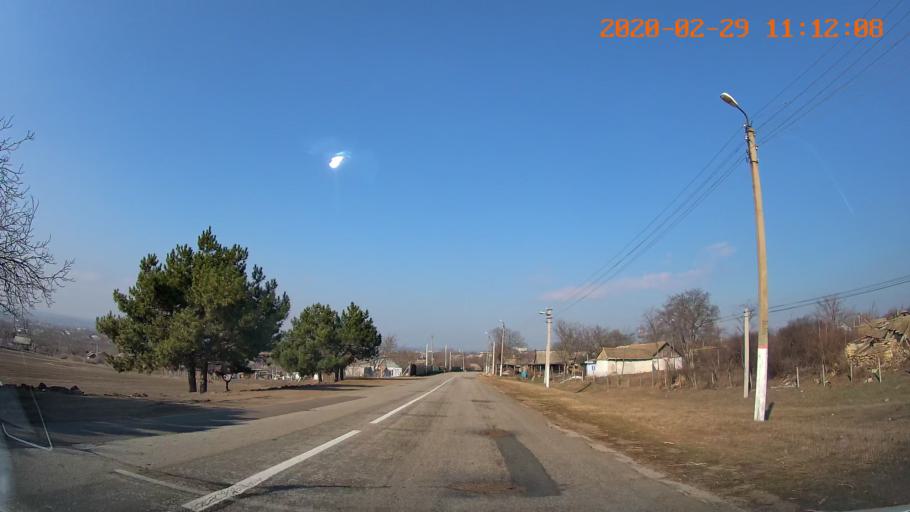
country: MD
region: Telenesti
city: Dubasari
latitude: 47.2601
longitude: 29.1886
